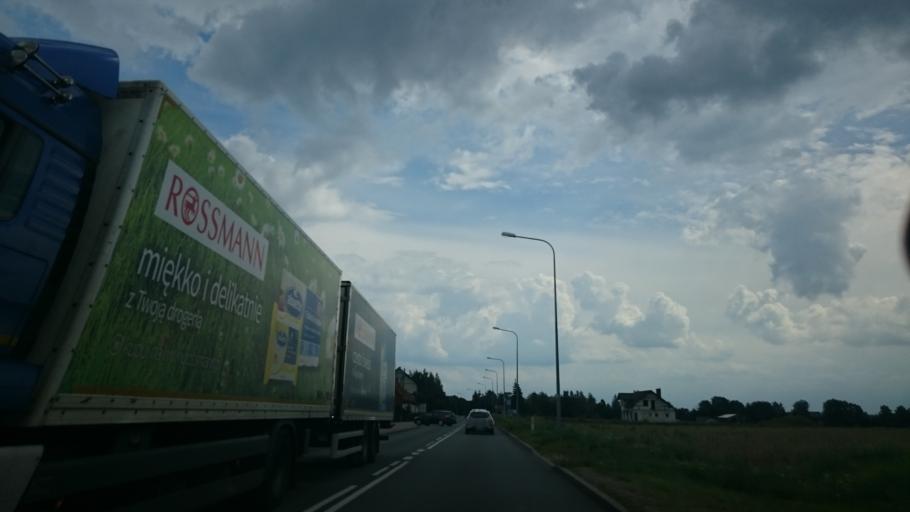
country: PL
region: Kujawsko-Pomorskie
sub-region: Powiat tucholski
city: Kesowo
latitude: 53.6525
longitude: 17.6959
